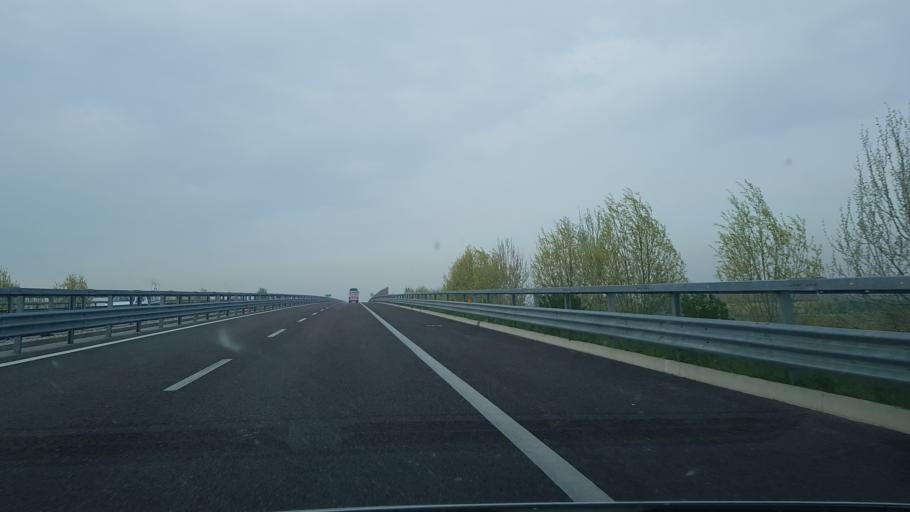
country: IT
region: Veneto
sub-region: Provincia di Vicenza
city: Albettone
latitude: 45.3518
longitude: 11.5932
